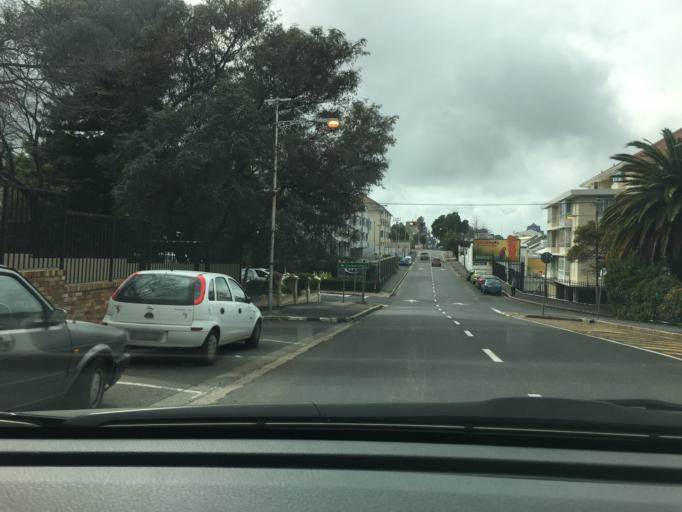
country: ZA
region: Western Cape
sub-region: City of Cape Town
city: Cape Town
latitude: -33.9283
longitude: 18.4089
